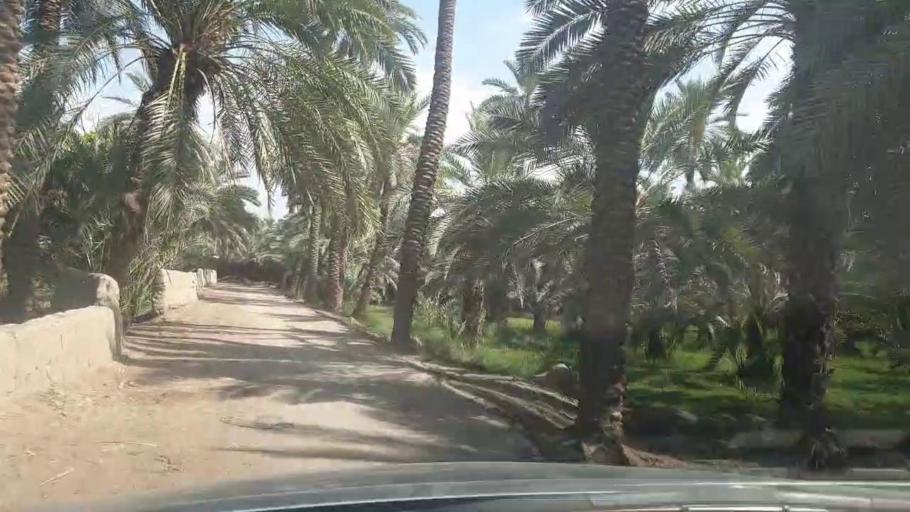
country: PK
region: Sindh
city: Khairpur
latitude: 27.5497
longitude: 68.7868
